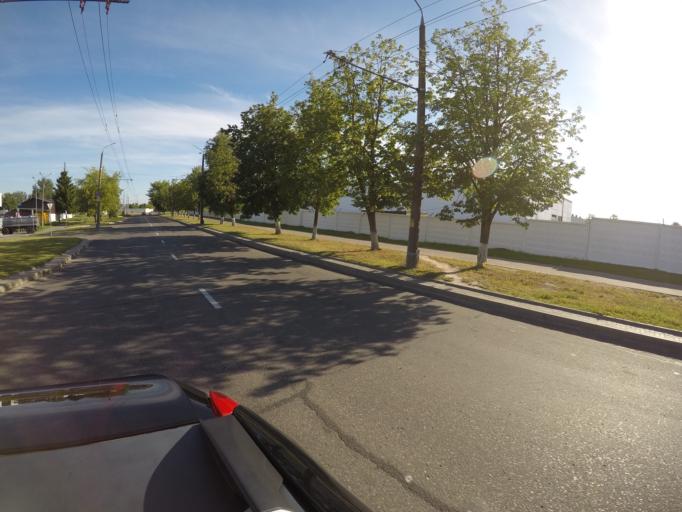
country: BY
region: Grodnenskaya
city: Hrodna
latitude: 53.7082
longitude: 23.8279
